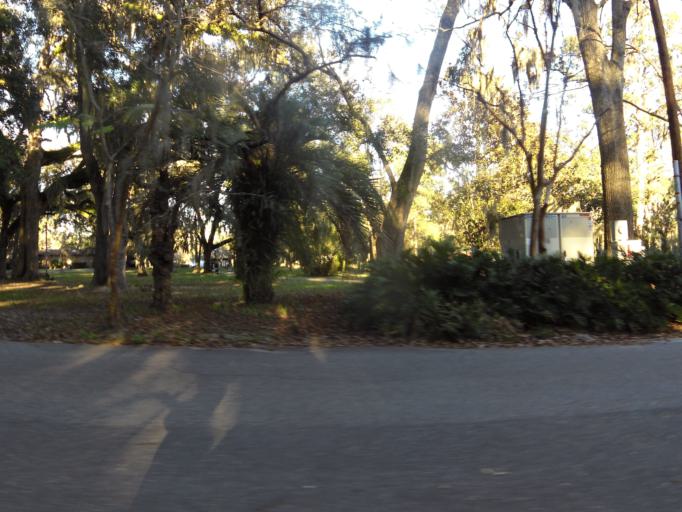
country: US
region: Florida
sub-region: Duval County
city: Jacksonville
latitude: 30.2713
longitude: -81.7058
